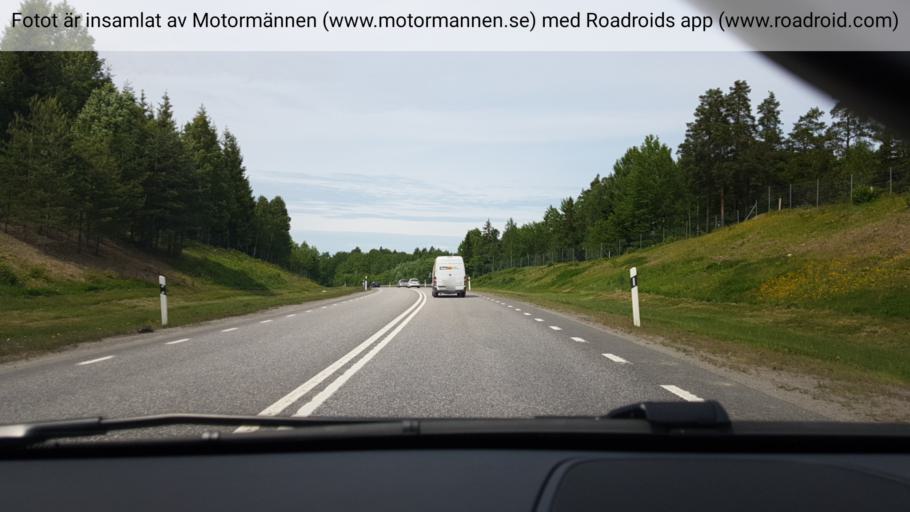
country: SE
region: Stockholm
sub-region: Huddinge Kommun
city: Huddinge
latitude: 59.1894
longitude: 18.0230
